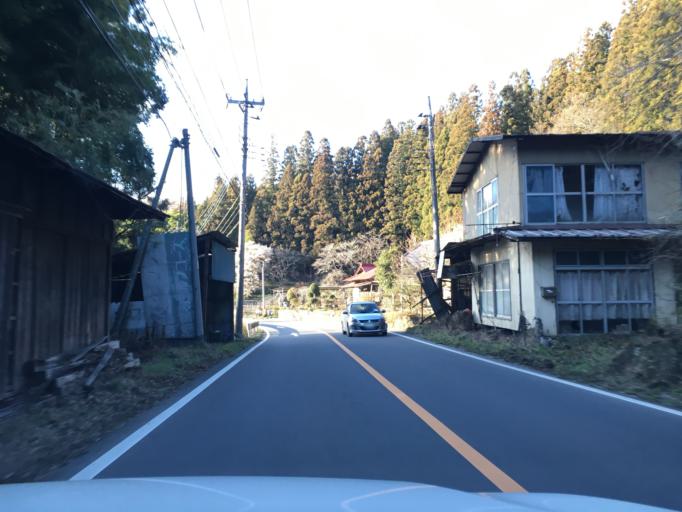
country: JP
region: Tochigi
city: Otawara
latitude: 36.8624
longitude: 140.1696
